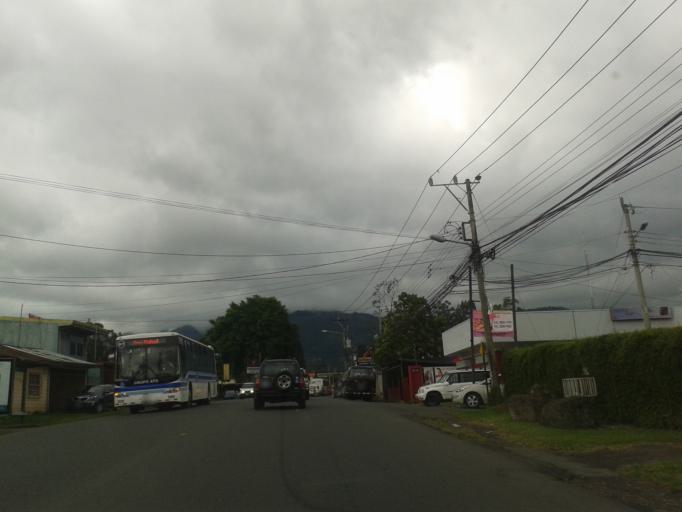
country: CR
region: San Jose
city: San Rafael Arriba
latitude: 9.8820
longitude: -84.0699
